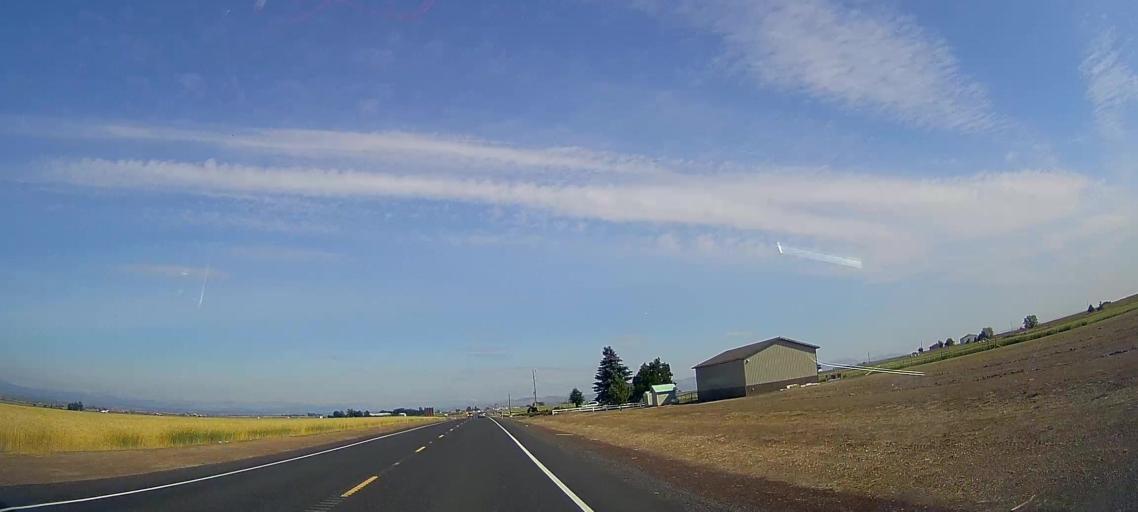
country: US
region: Oregon
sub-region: Jefferson County
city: Madras
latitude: 44.6744
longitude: -121.1428
